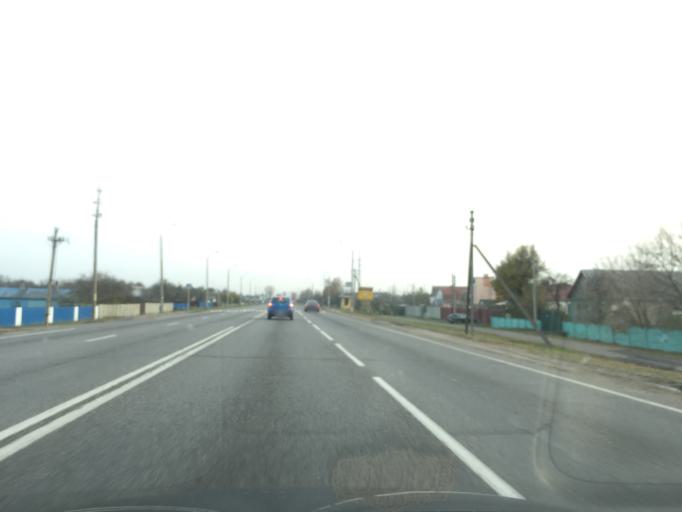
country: BY
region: Gomel
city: Kastsyukowka
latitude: 52.4947
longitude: 30.9600
